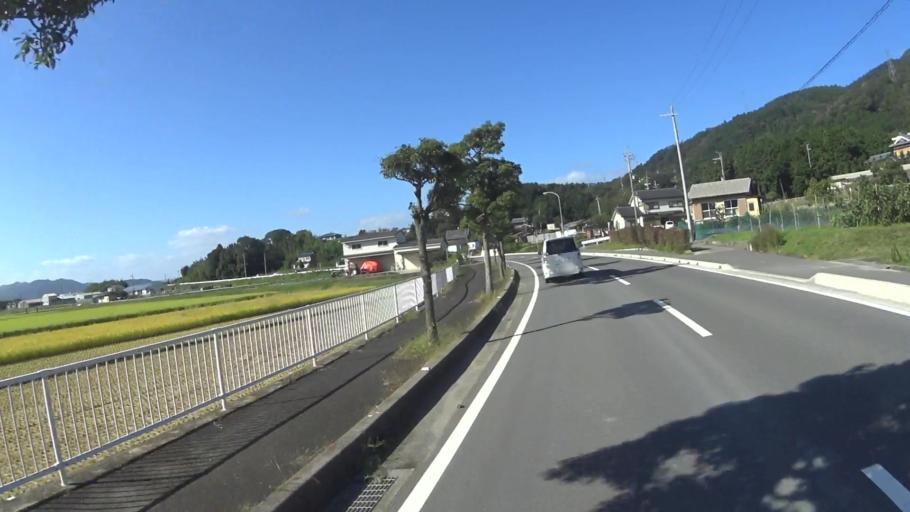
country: JP
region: Kyoto
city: Kameoka
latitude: 35.0327
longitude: 135.5831
